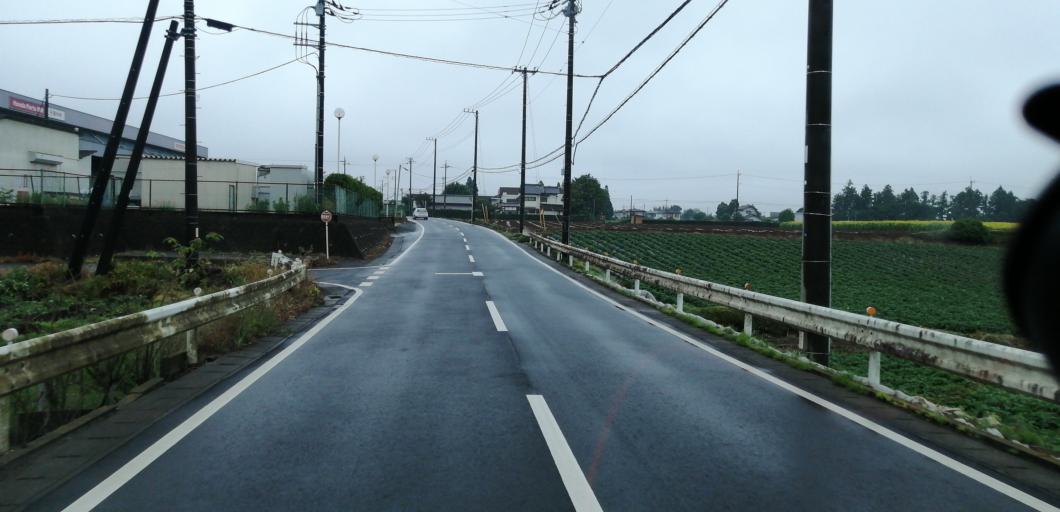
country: JP
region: Chiba
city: Yachimata
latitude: 35.6043
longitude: 140.2781
